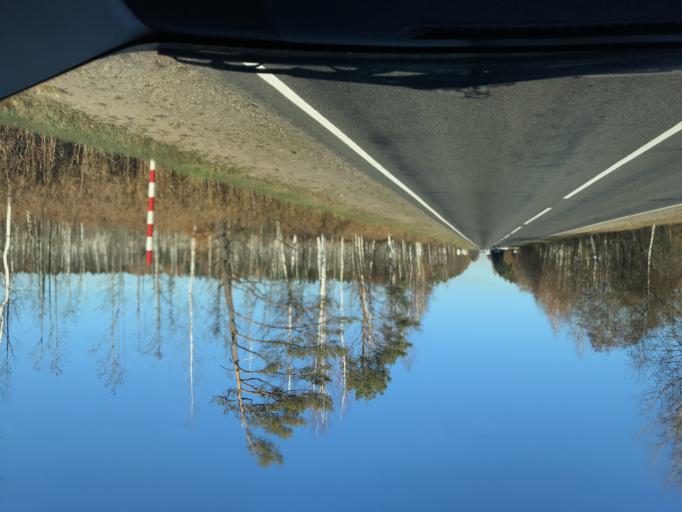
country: BY
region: Vitebsk
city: Polatsk
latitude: 55.4322
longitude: 28.7825
